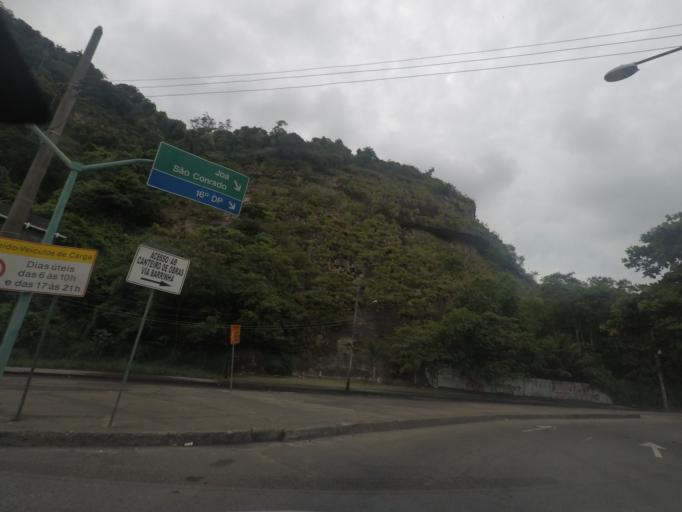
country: BR
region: Rio de Janeiro
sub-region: Rio De Janeiro
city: Rio de Janeiro
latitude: -23.0072
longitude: -43.3029
